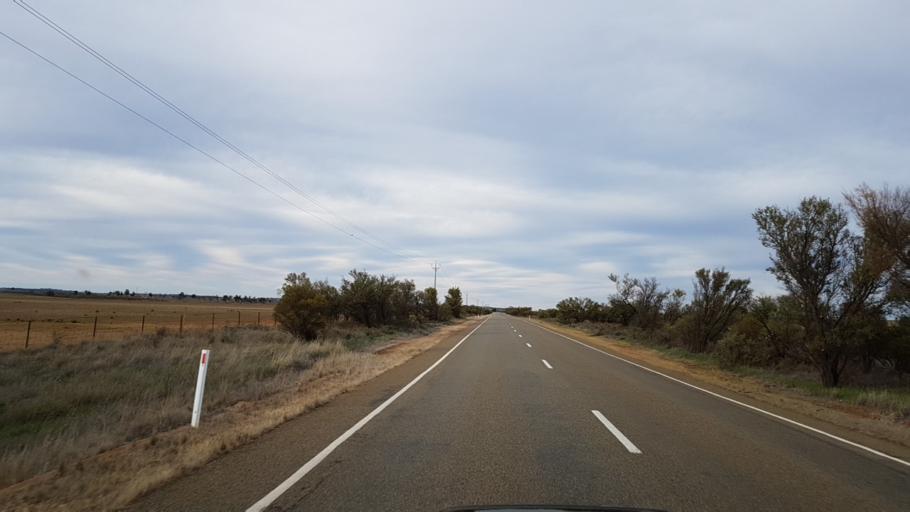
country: AU
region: South Australia
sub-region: Peterborough
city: Peterborough
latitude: -32.9974
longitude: 138.7819
